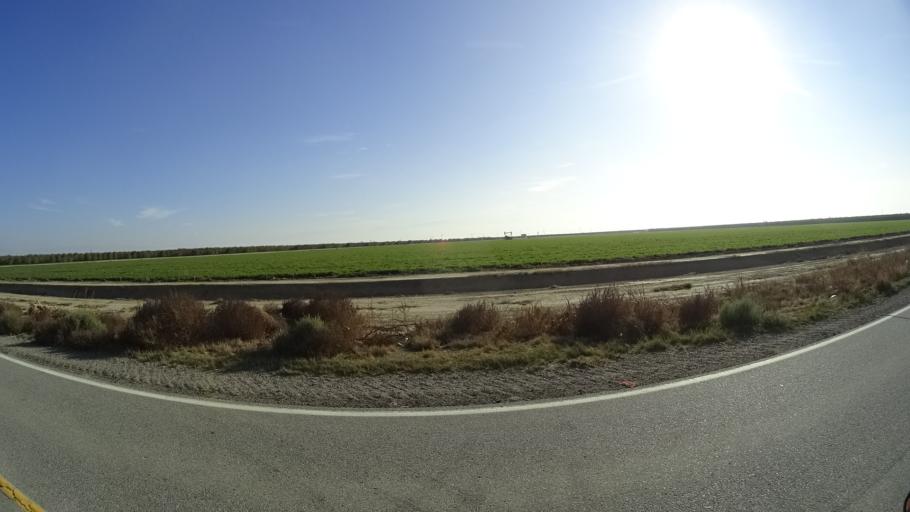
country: US
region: California
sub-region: Kern County
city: Rosedale
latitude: 35.2963
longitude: -119.1414
